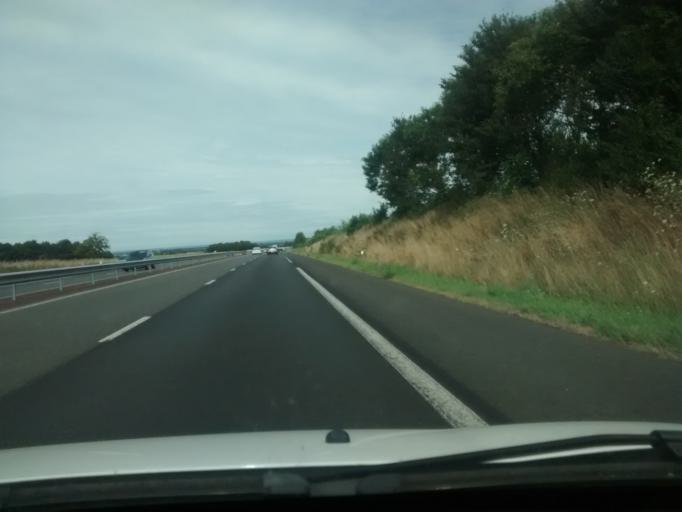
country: FR
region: Lower Normandy
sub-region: Departement de la Manche
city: Saint-James
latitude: 48.5001
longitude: -1.3440
